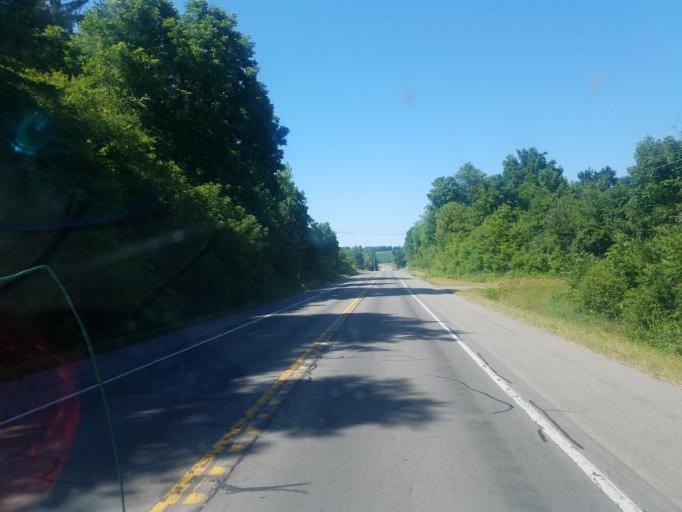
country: US
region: New York
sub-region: Ontario County
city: Phelps
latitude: 42.9714
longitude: -77.0758
